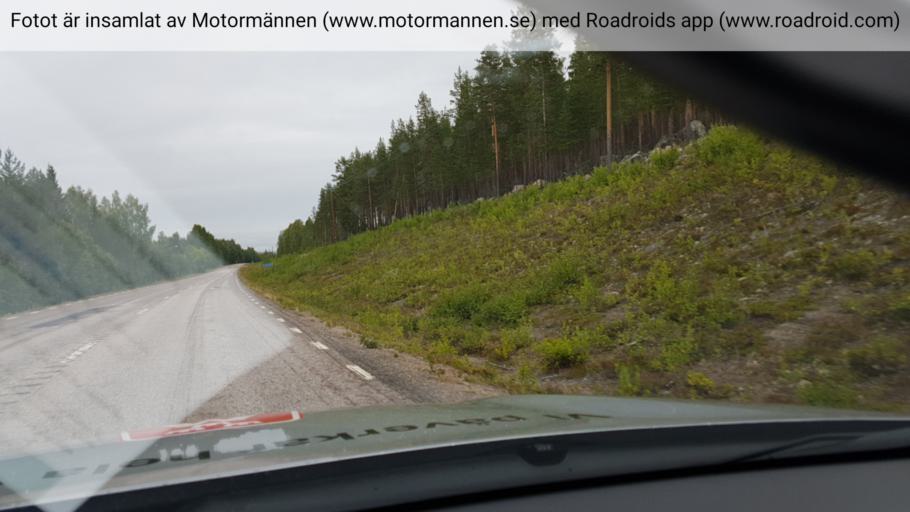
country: SE
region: Norrbotten
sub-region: Alvsbyns Kommun
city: AElvsbyn
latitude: 66.1813
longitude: 20.8776
